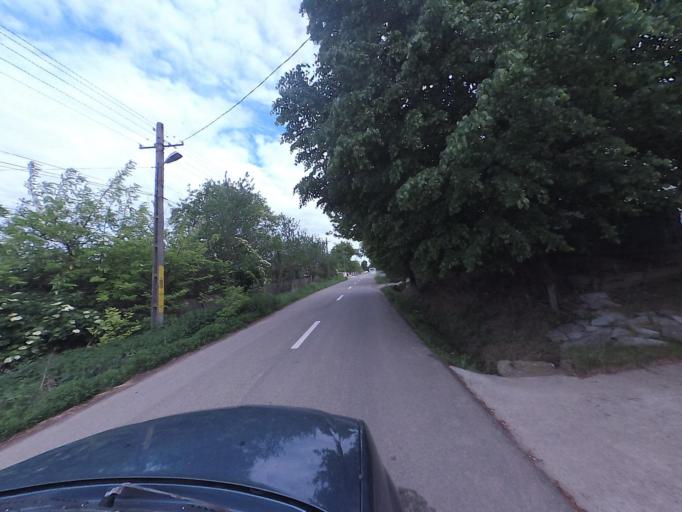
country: RO
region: Neamt
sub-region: Comuna Dulcesti
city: Dulcesti
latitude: 46.9602
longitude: 26.7864
